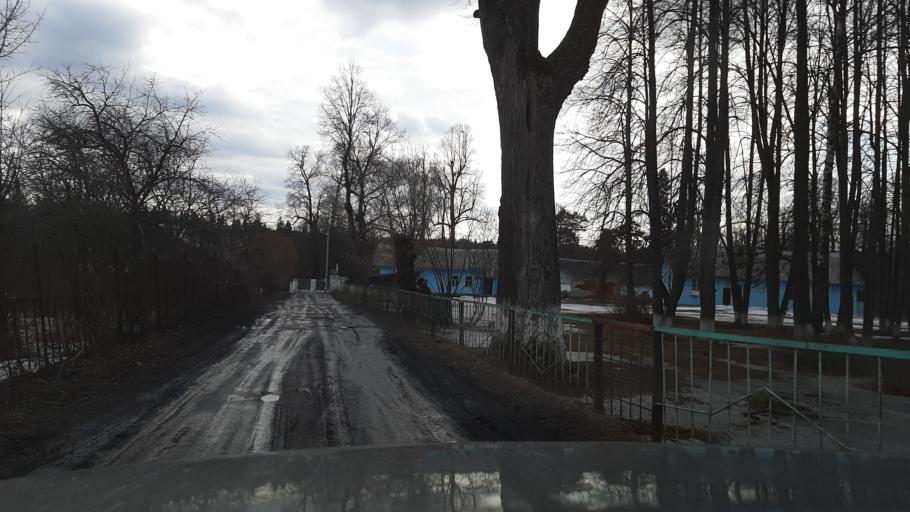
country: RU
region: Ivanovo
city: Teykovo
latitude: 56.8978
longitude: 40.6641
